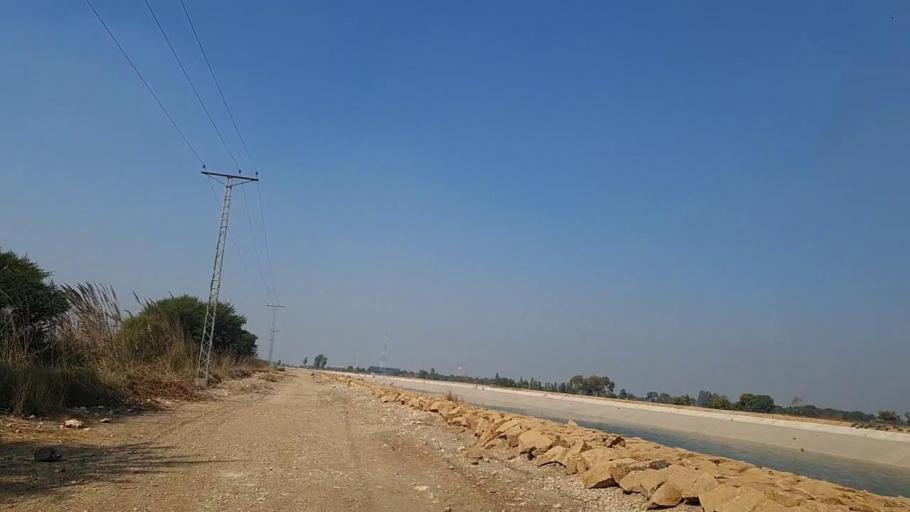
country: PK
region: Sindh
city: Sakrand
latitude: 26.2398
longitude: 68.2752
